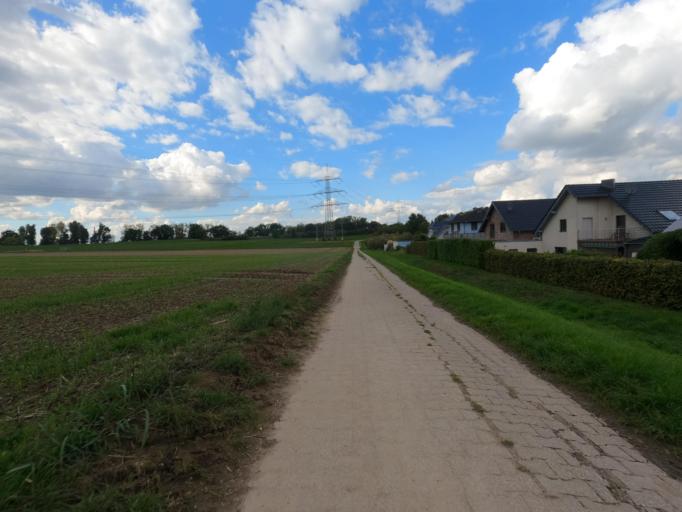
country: DE
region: North Rhine-Westphalia
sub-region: Regierungsbezirk Koln
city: Aldenhoven
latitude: 50.9299
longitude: 6.3114
